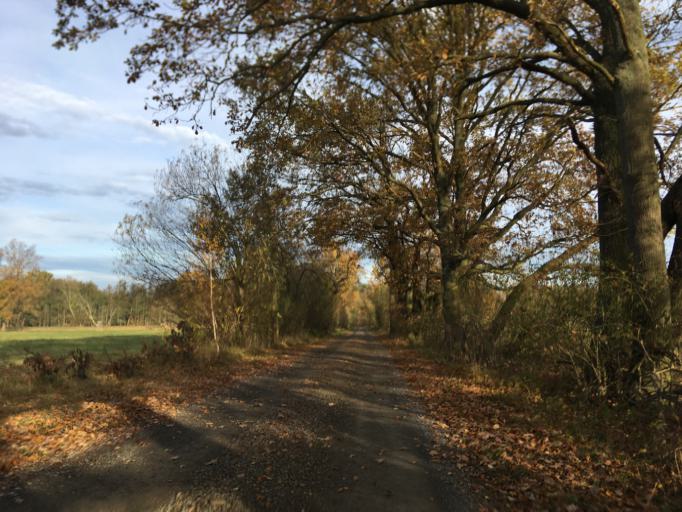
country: DE
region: Brandenburg
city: Luebben
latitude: 51.9851
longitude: 13.8727
